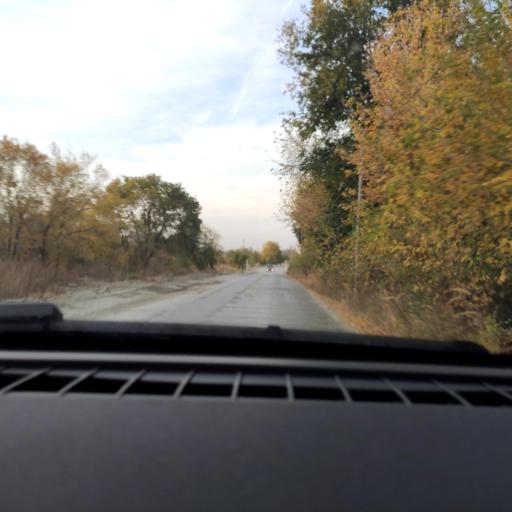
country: RU
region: Voronezj
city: Maslovka
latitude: 51.6022
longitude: 39.2587
